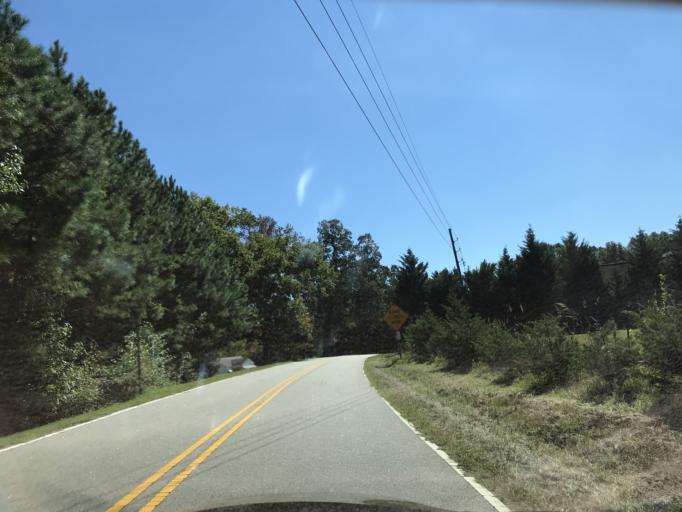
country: US
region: North Carolina
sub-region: Wake County
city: Wake Forest
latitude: 35.9475
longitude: -78.5904
